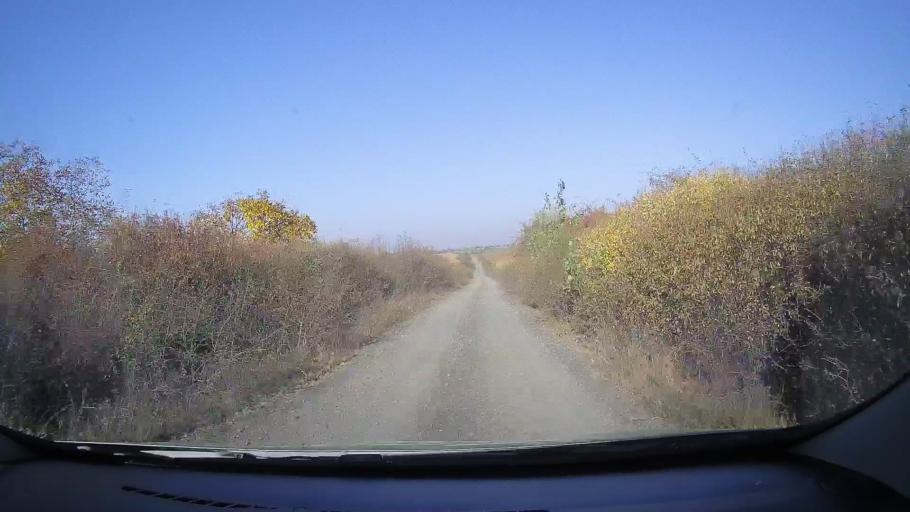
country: RO
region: Satu Mare
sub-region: Comuna Sauca
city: Sauca
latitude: 47.4795
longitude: 22.4714
